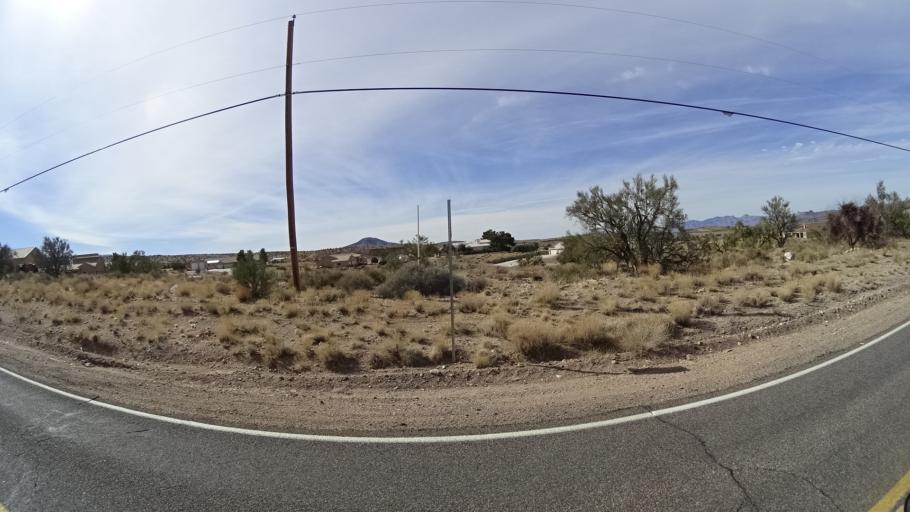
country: US
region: Arizona
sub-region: Mohave County
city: Kingman
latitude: 35.1728
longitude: -113.9836
